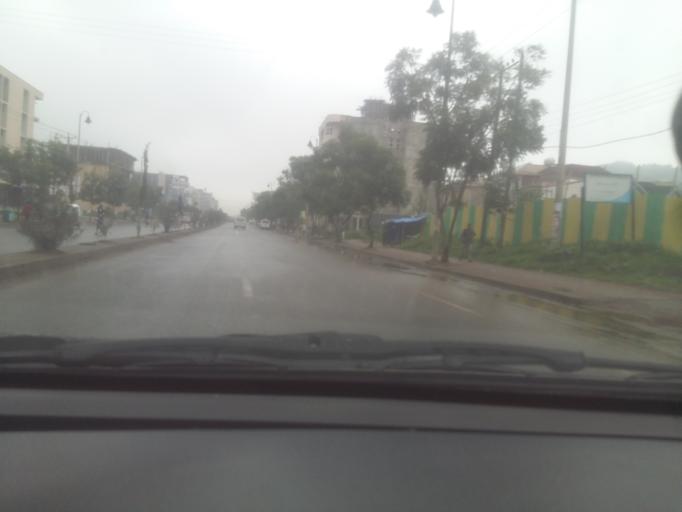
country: ET
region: Adis Abeba
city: Addis Ababa
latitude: 8.9490
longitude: 38.7241
